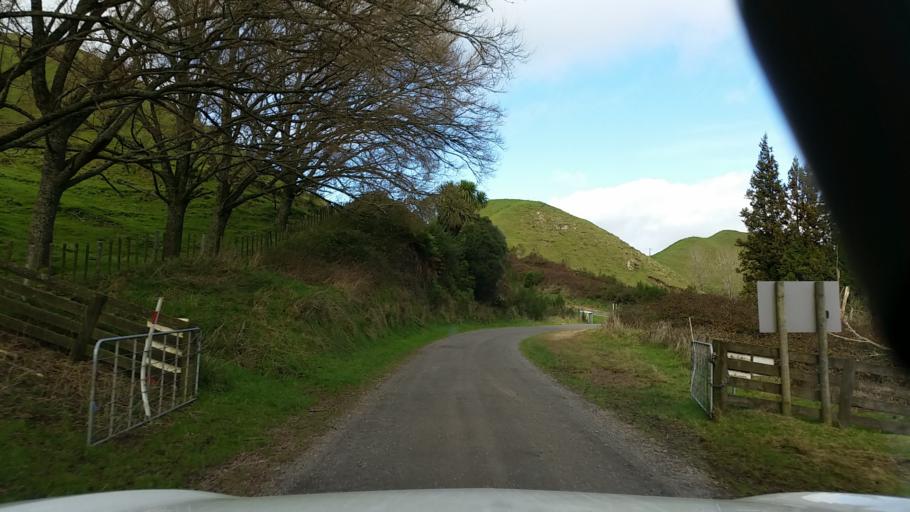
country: NZ
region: Waikato
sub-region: Taupo District
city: Taupo
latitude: -38.4640
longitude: 176.2418
